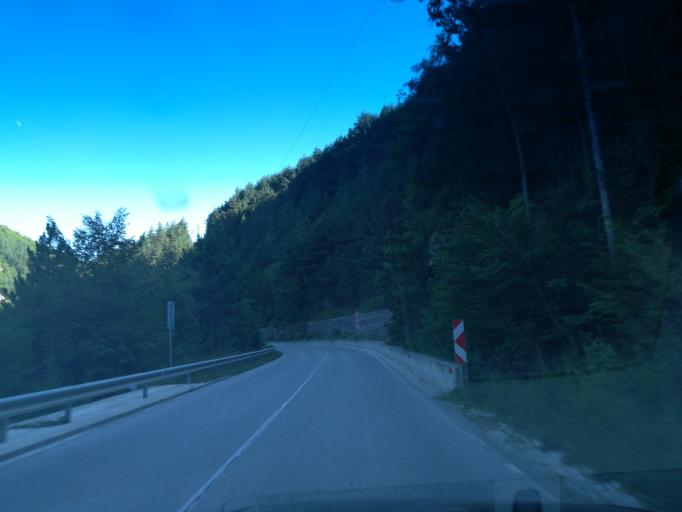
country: BG
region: Plovdiv
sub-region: Obshtina Luki
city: Luki
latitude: 41.8814
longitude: 24.6941
